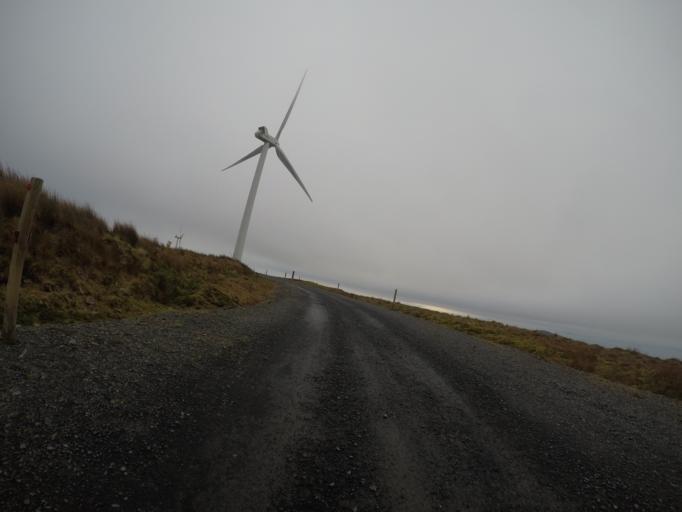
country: GB
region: Scotland
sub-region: North Ayrshire
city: Fairlie
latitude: 55.7445
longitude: -4.7972
